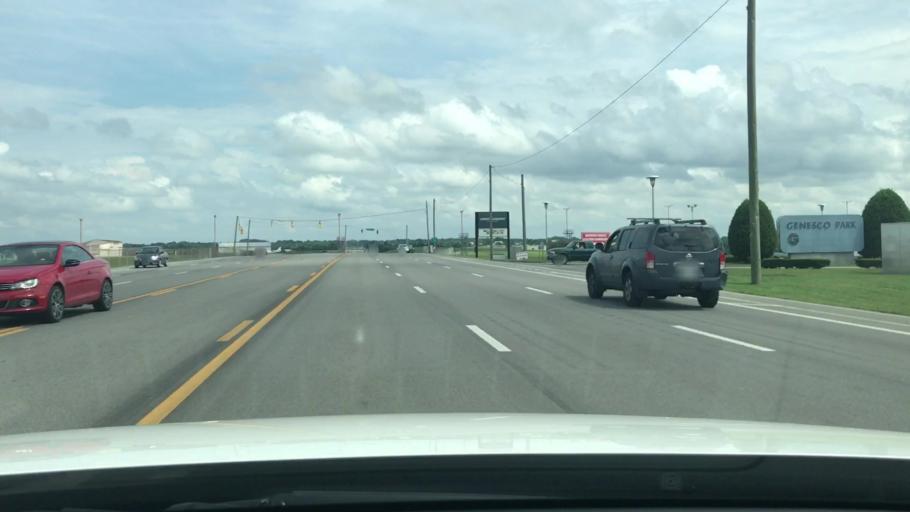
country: US
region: Tennessee
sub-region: Davidson County
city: Oak Hill
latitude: 36.1136
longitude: -86.6907
